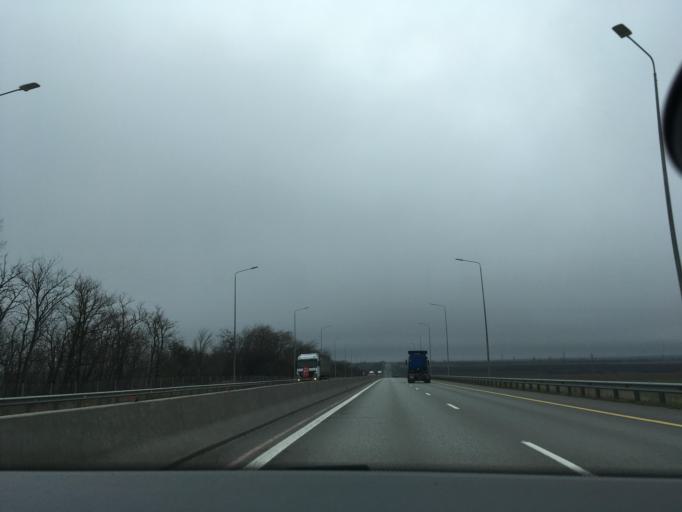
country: RU
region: Rostov
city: Samarskoye
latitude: 46.9629
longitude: 39.7182
